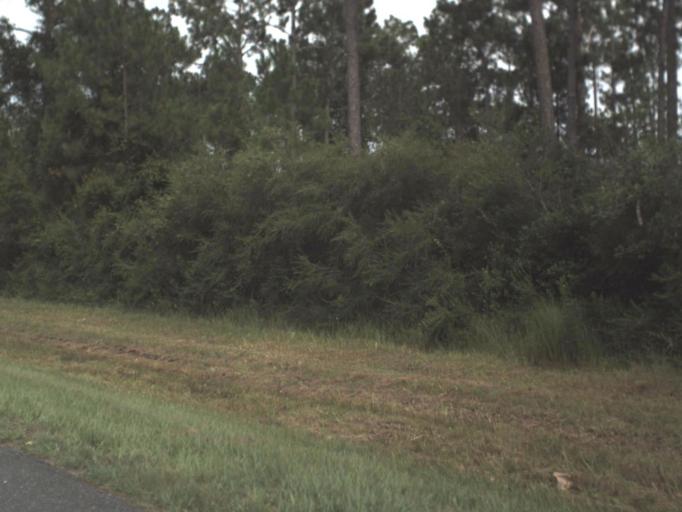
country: US
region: Florida
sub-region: Taylor County
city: Perry
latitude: 30.1067
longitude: -83.4296
